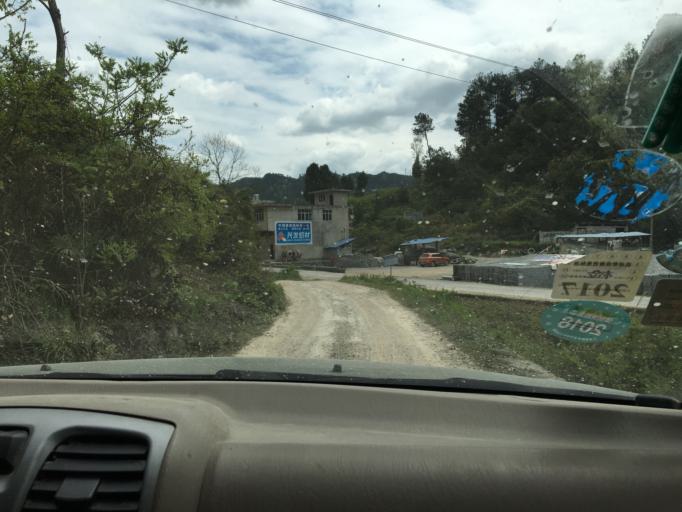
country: CN
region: Guizhou Sheng
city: Kuanping
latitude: 28.0197
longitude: 108.0767
